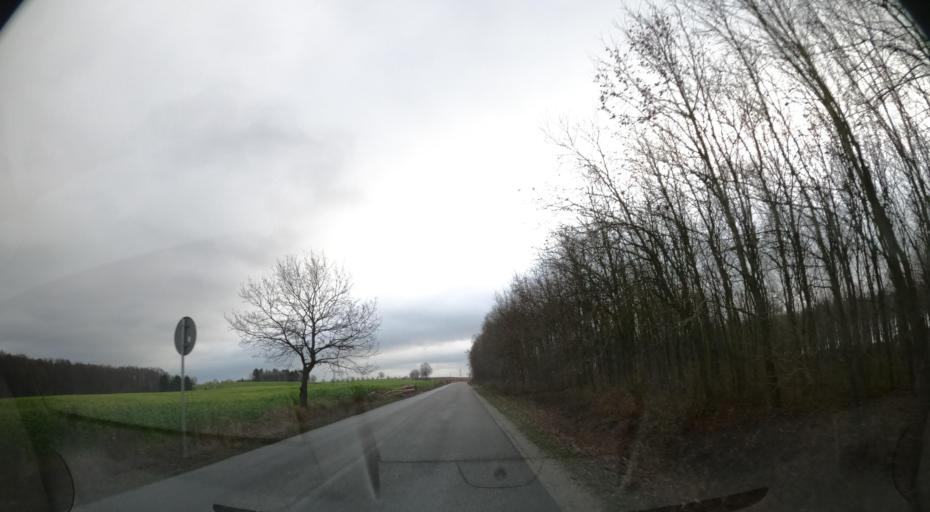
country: PL
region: Kujawsko-Pomorskie
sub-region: Powiat nakielski
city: Sadki
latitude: 53.1871
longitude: 17.3966
